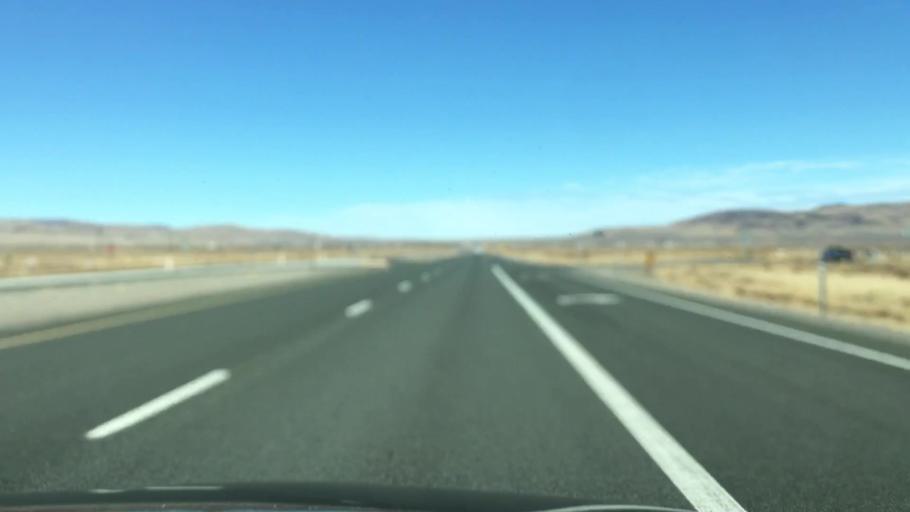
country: US
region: Nevada
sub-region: Lyon County
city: Stagecoach
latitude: 39.3421
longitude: -119.4268
